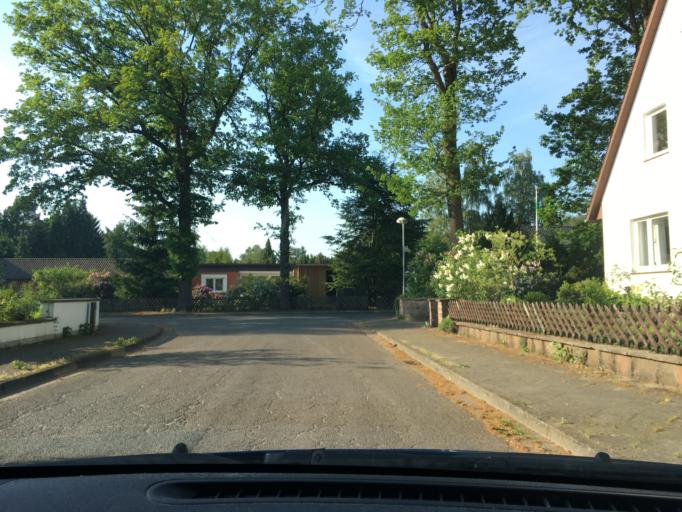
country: DE
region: Lower Saxony
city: Lueneburg
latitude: 53.2314
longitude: 10.4209
